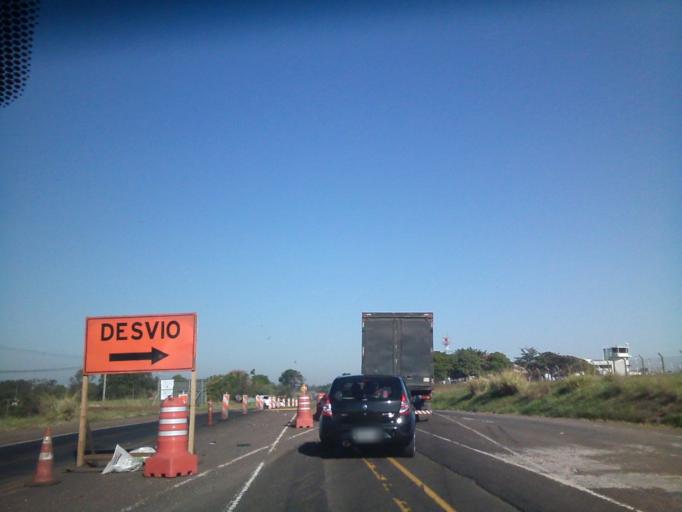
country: BR
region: Sao Paulo
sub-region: Presidente Prudente
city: Presidente Prudente
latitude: -22.1780
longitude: -51.4140
